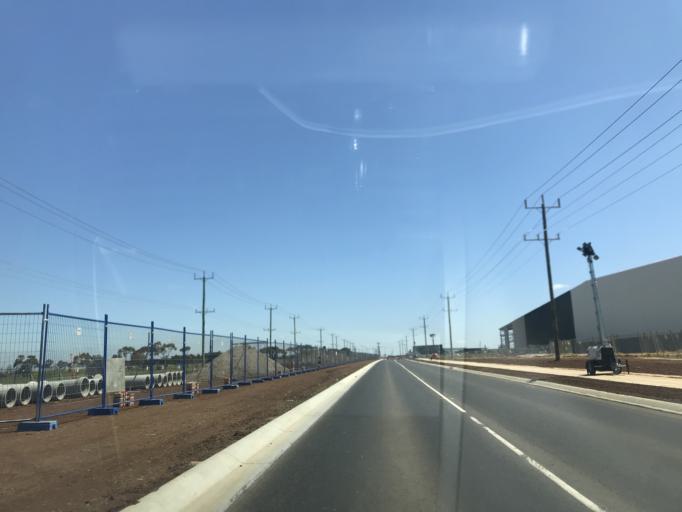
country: AU
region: Victoria
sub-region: Wyndham
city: Truganina
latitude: -37.8405
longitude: 144.7557
